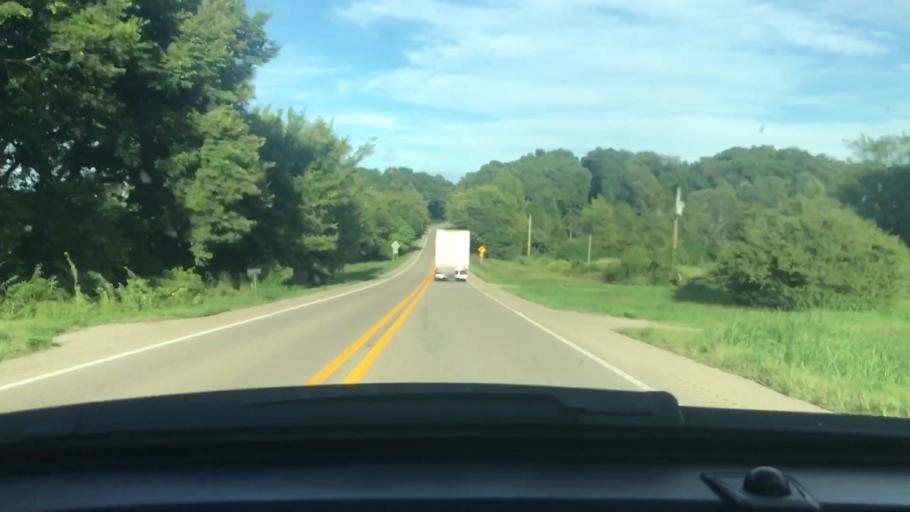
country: US
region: Arkansas
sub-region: Randolph County
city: Pocahontas
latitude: 36.2125
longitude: -91.2108
